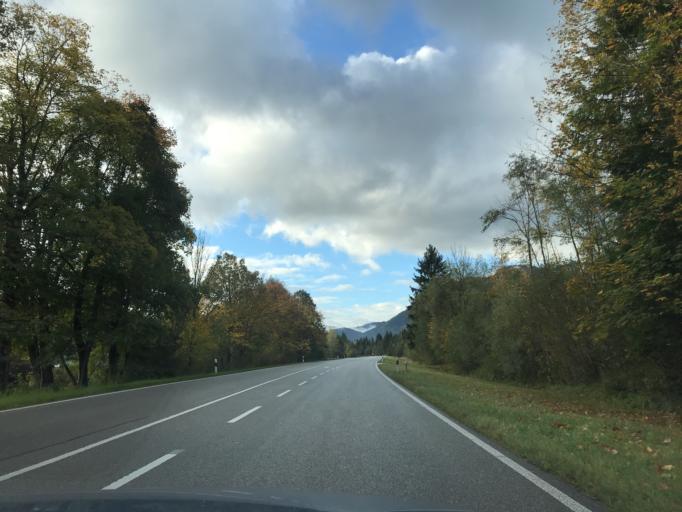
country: DE
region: Bavaria
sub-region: Upper Bavaria
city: Lenggries
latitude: 47.7070
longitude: 11.5625
